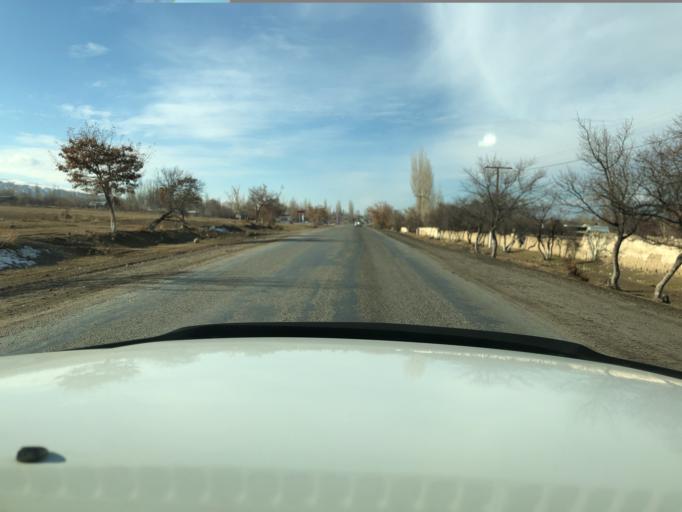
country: KG
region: Ysyk-Koel
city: Pokrovka
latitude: 42.3257
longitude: 77.9442
